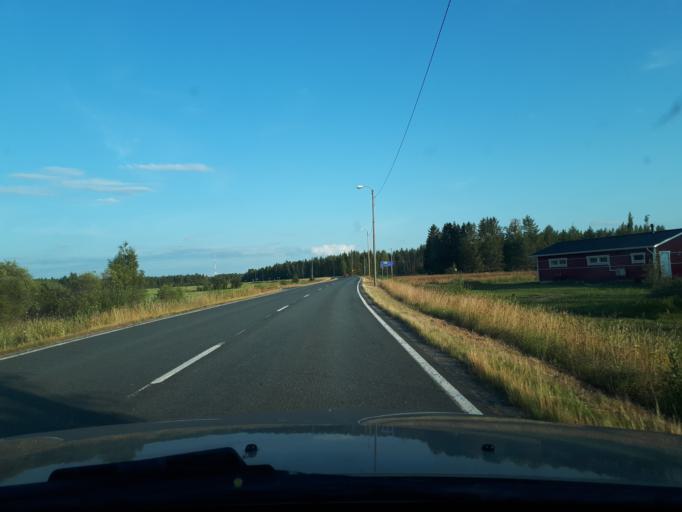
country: FI
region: Northern Ostrobothnia
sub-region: Oulu
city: Oulunsalo
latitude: 64.9821
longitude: 25.2710
